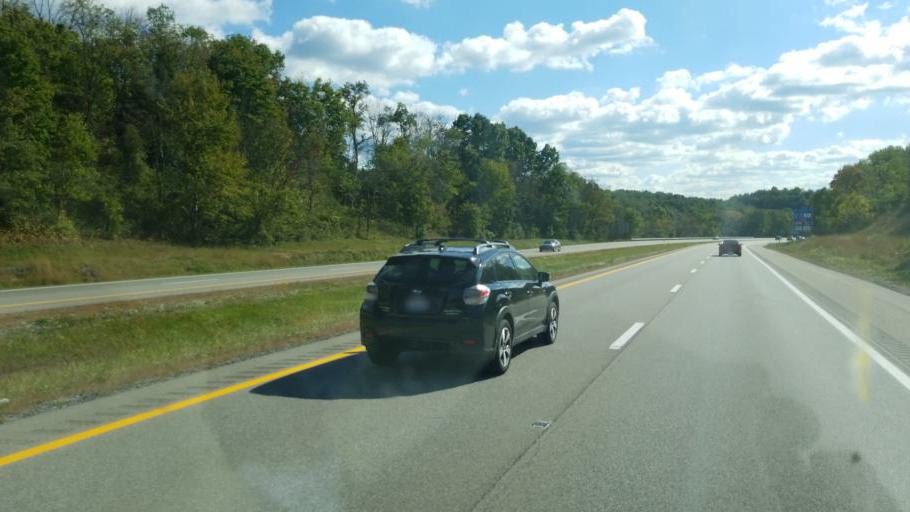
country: US
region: West Virginia
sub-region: Monongalia County
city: Brookhaven
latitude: 39.6320
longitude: -79.9004
